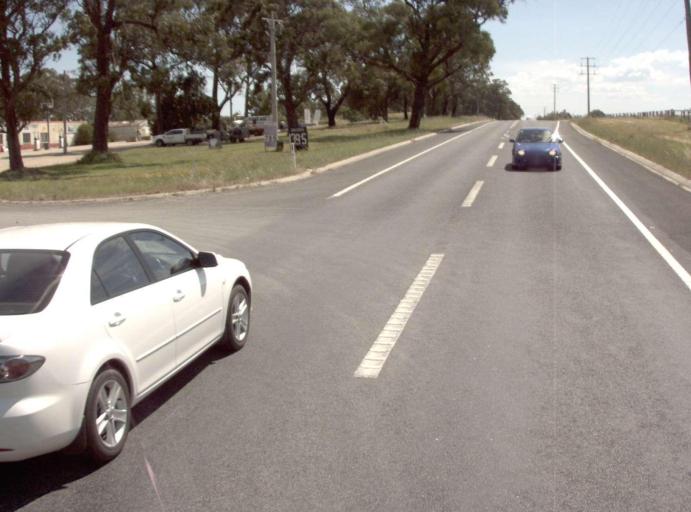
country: AU
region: Victoria
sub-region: East Gippsland
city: Bairnsdale
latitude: -37.9049
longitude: 147.3365
